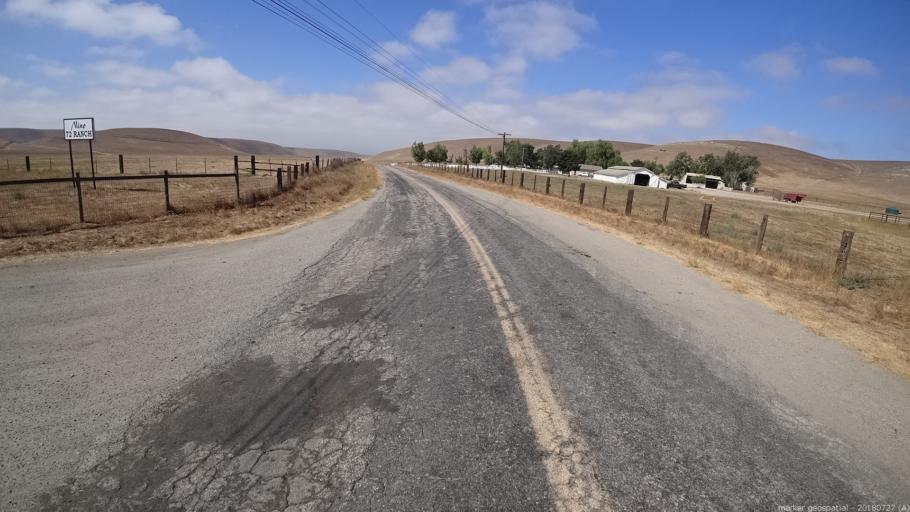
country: US
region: California
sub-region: Monterey County
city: King City
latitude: 36.2449
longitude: -121.0363
